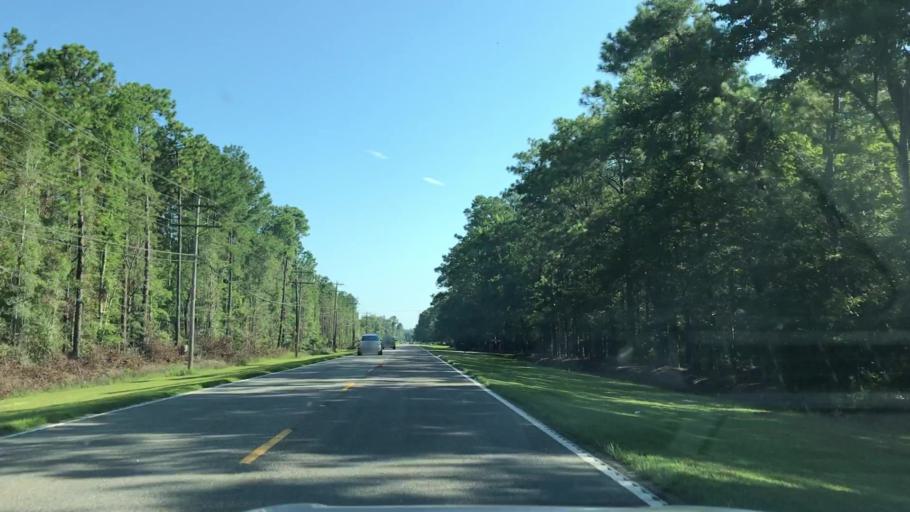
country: US
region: South Carolina
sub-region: Georgetown County
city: Georgetown
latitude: 33.4228
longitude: -79.2817
